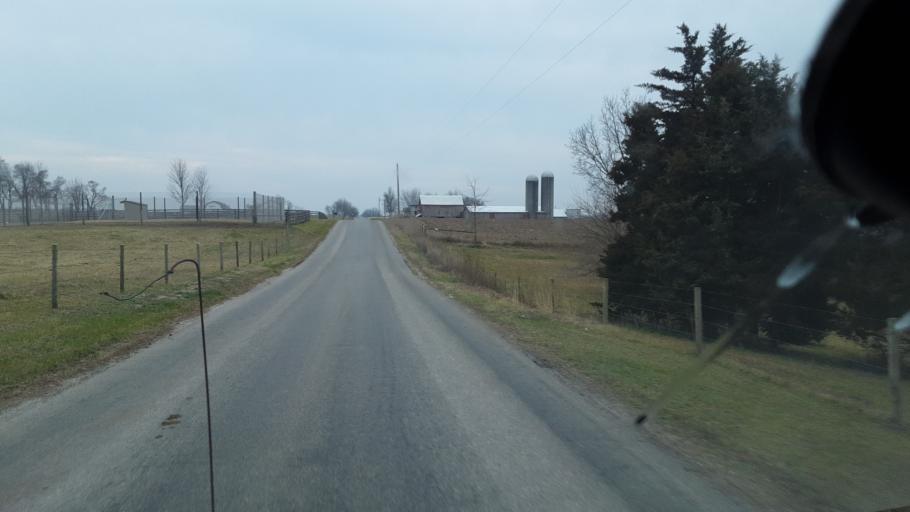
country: US
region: Michigan
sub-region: Saint Joseph County
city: White Pigeon
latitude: 41.7125
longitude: -85.6206
